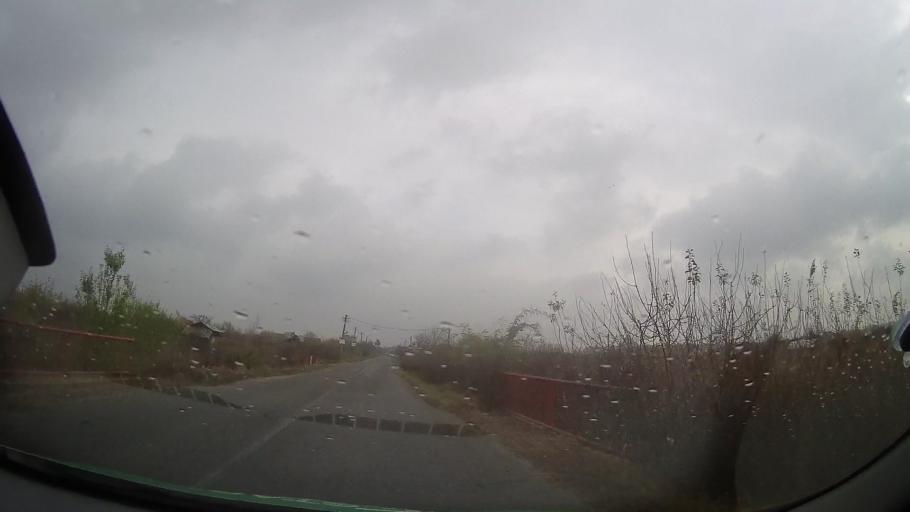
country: RO
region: Prahova
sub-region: Comuna Draganesti
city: Draganesti
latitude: 44.8299
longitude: 26.2766
